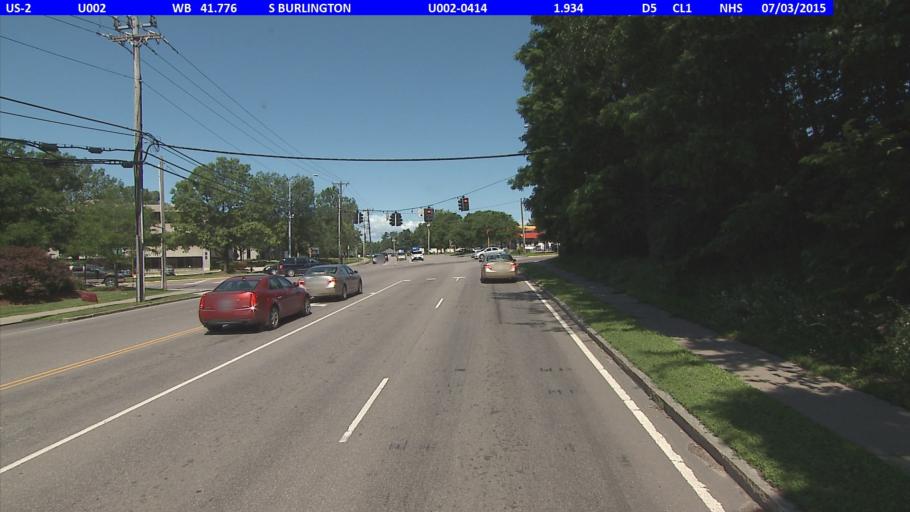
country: US
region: Vermont
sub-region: Chittenden County
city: South Burlington
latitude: 44.4627
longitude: -73.1534
